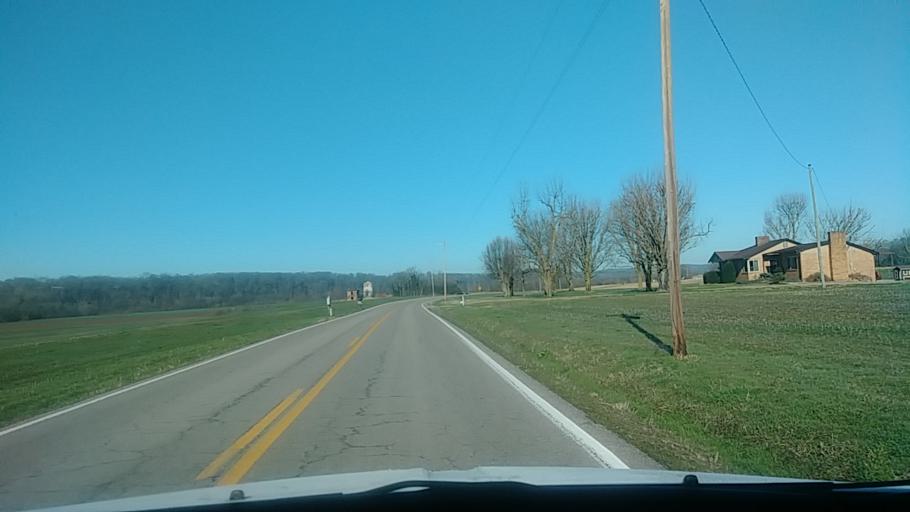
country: US
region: Tennessee
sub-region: Jefferson County
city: White Pine
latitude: 36.1511
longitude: -83.1552
